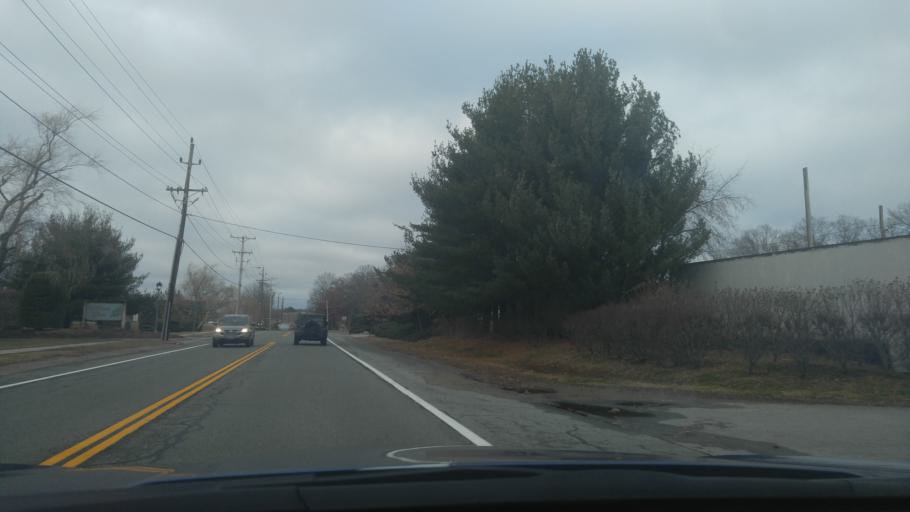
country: US
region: Rhode Island
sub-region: Kent County
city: Warwick
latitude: 41.7060
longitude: -71.3983
